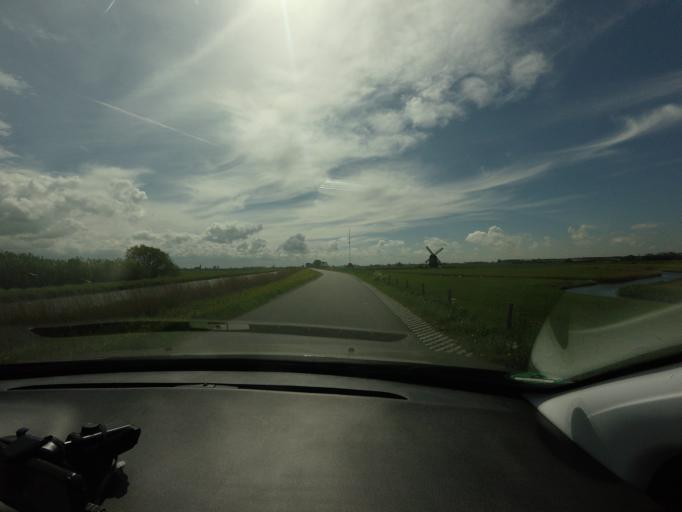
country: NL
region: North Holland
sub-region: Gemeente Heerhugowaard
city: Heerhugowaard
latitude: 52.6189
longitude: 4.8860
